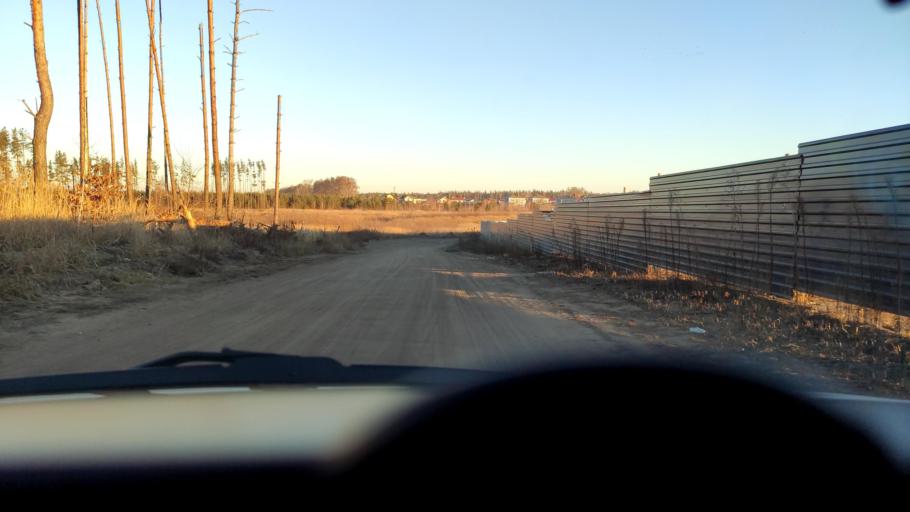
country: RU
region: Voronezj
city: Podgornoye
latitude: 51.7503
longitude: 39.1366
